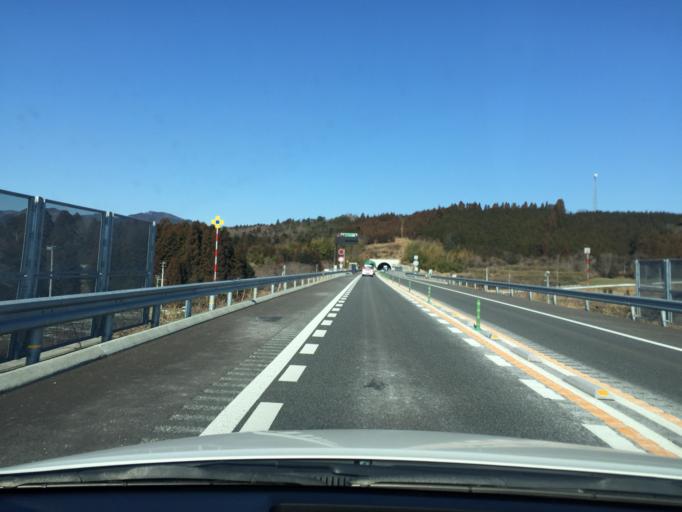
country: JP
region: Fukushima
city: Namie
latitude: 37.5850
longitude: 140.9337
